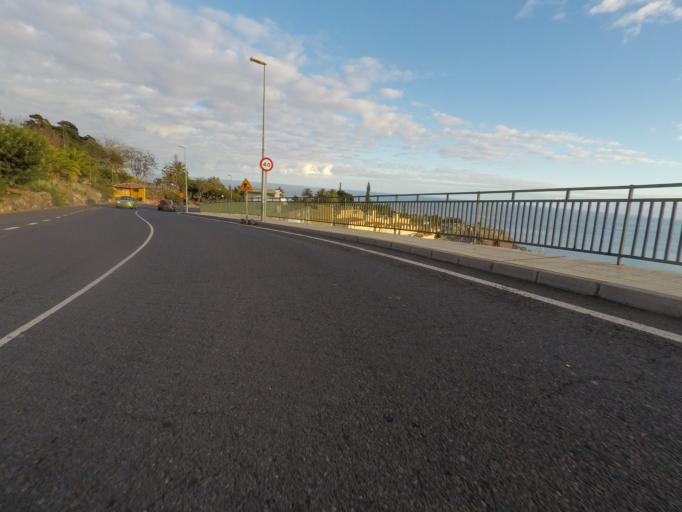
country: ES
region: Canary Islands
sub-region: Provincia de Santa Cruz de Tenerife
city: Alajero
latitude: 28.0348
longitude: -17.1921
